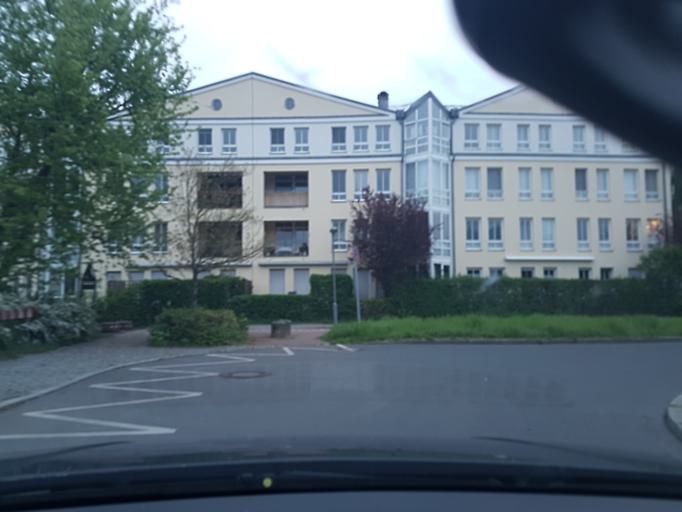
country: DE
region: Berlin
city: Mariendorf
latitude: 52.4292
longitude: 13.4055
